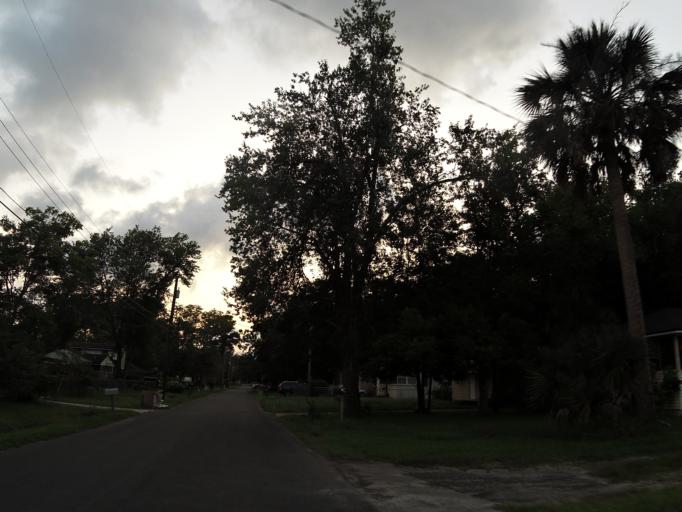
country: US
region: Florida
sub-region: Duval County
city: Jacksonville
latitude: 30.3310
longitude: -81.7229
